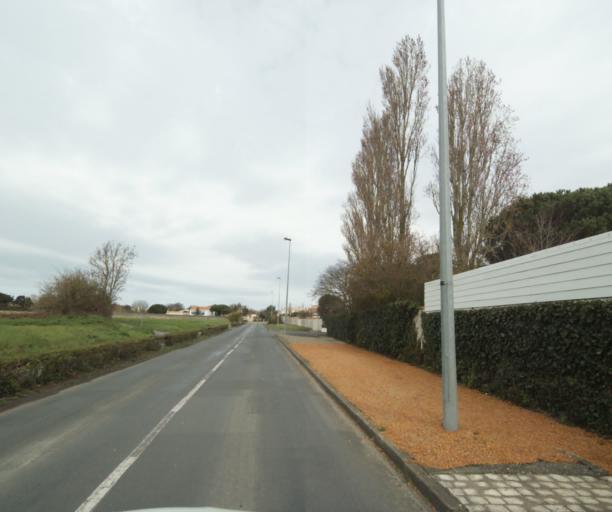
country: FR
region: Poitou-Charentes
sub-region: Departement de la Charente-Maritime
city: Lagord
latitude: 46.1830
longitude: -1.1668
